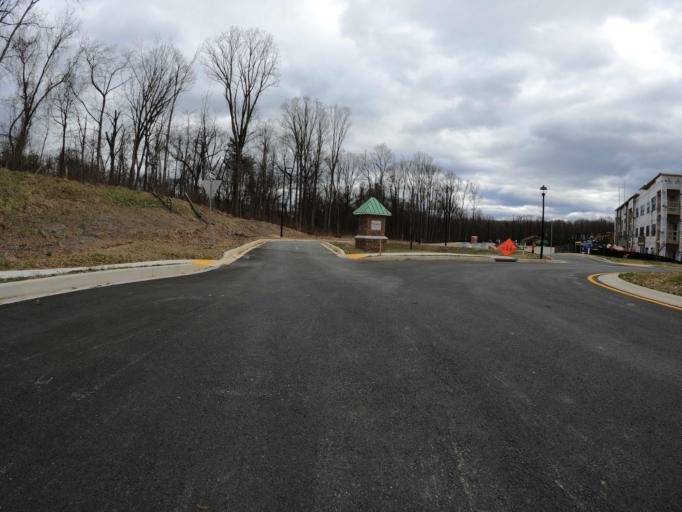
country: US
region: Maryland
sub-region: Howard County
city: Columbia
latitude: 39.2975
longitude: -76.8664
